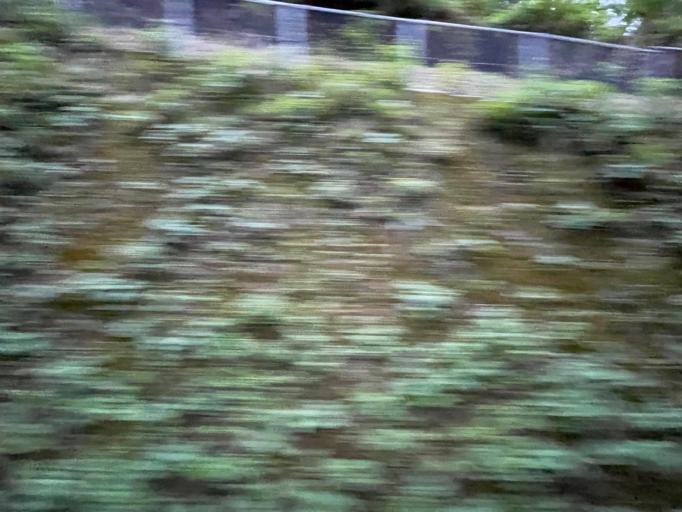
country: JP
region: Tochigi
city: Karasuyama
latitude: 36.6483
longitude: 140.1324
